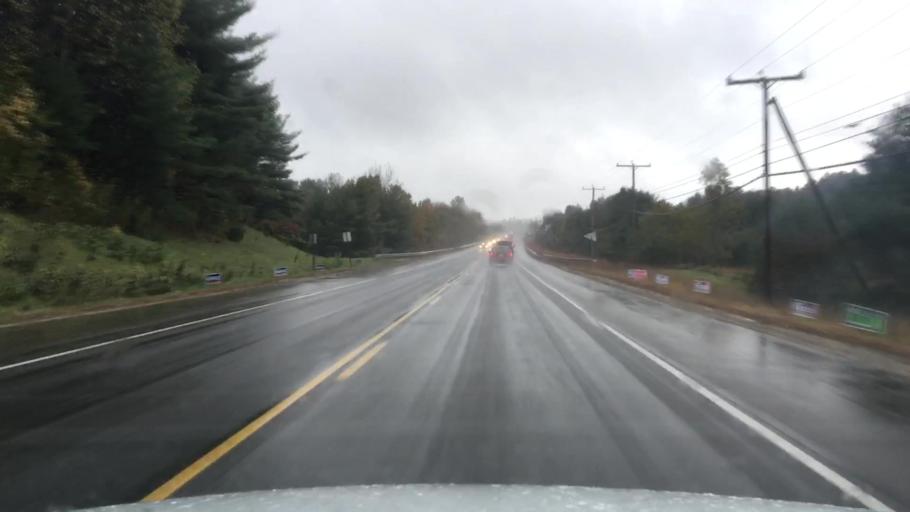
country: US
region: New Hampshire
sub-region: Strafford County
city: Rochester
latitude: 43.2650
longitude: -70.9791
